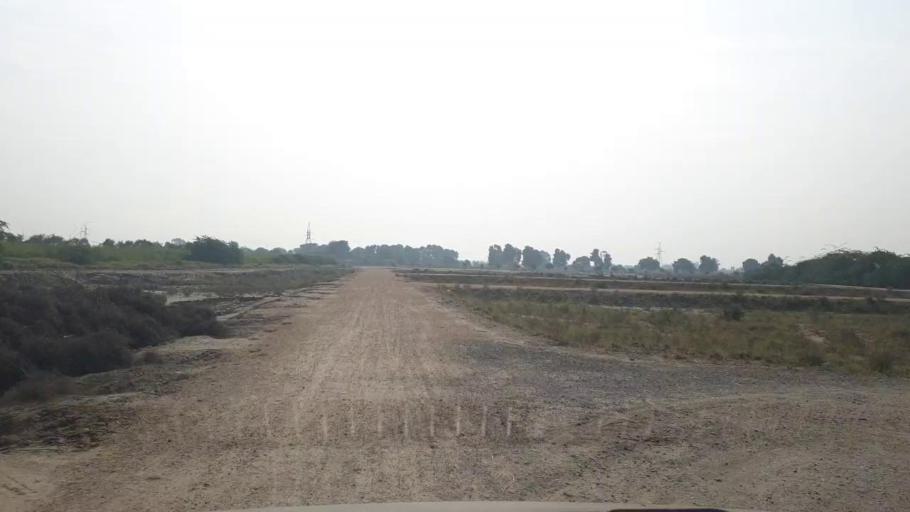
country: PK
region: Sindh
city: Tando Muhammad Khan
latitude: 25.1350
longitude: 68.5213
